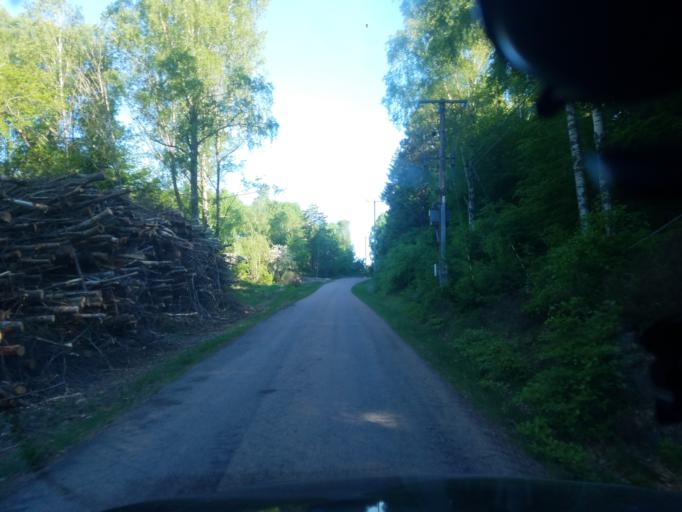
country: SE
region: Vaestra Goetaland
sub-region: Orust
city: Henan
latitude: 58.2797
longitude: 11.6389
